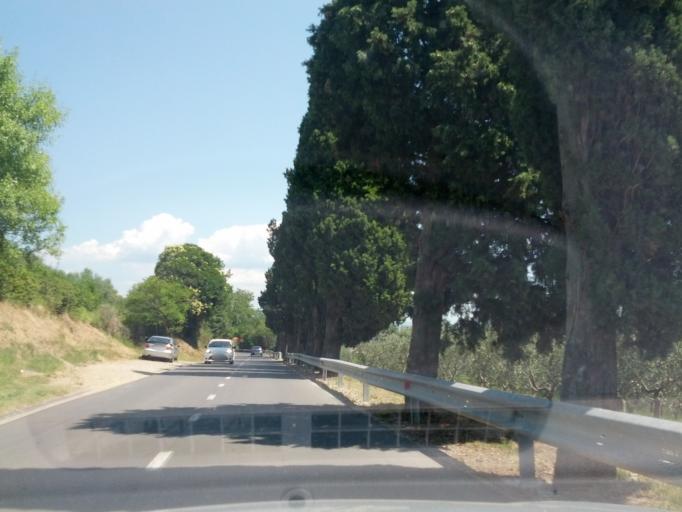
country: SI
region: Koper-Capodistria
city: Ankaran
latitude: 45.5849
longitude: 13.7141
